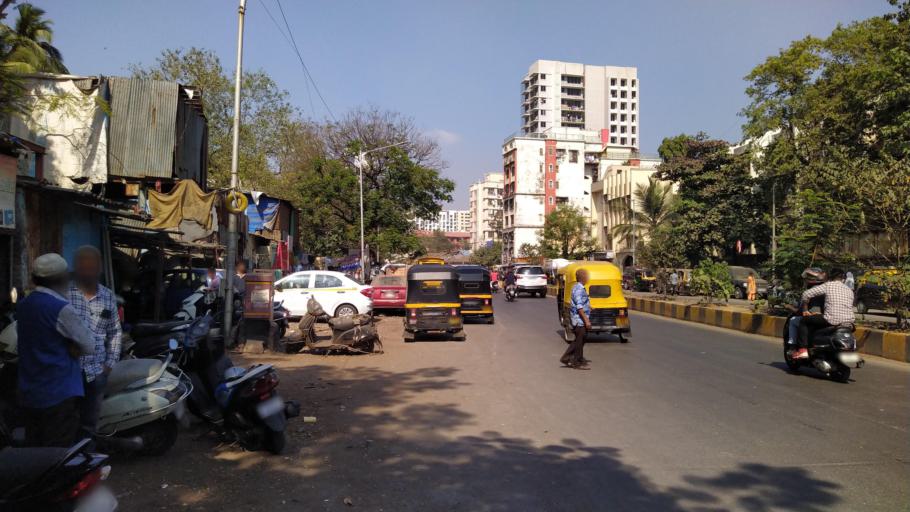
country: IN
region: Maharashtra
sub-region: Mumbai Suburban
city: Mumbai
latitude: 19.0642
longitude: 72.8742
